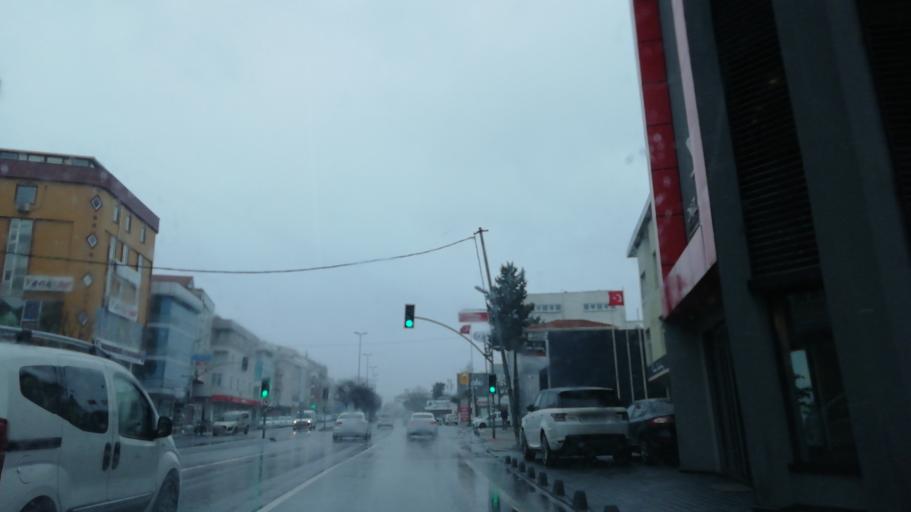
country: TR
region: Istanbul
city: Yakuplu
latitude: 41.0009
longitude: 28.7121
